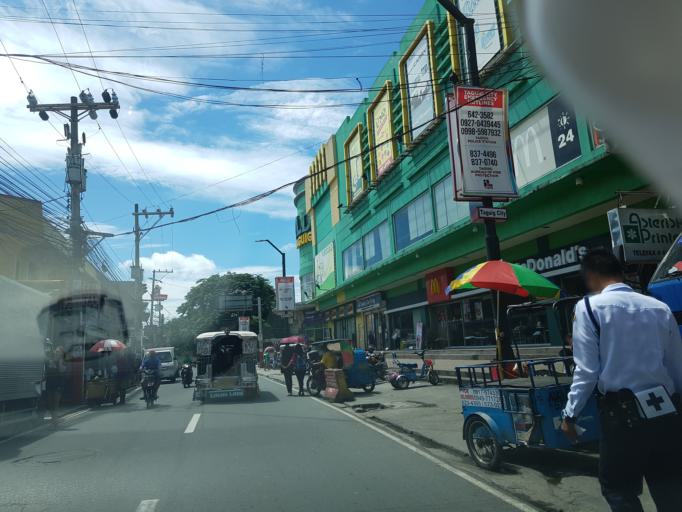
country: PH
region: Calabarzon
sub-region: Province of Rizal
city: Pateros
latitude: 14.5304
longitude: 121.0696
